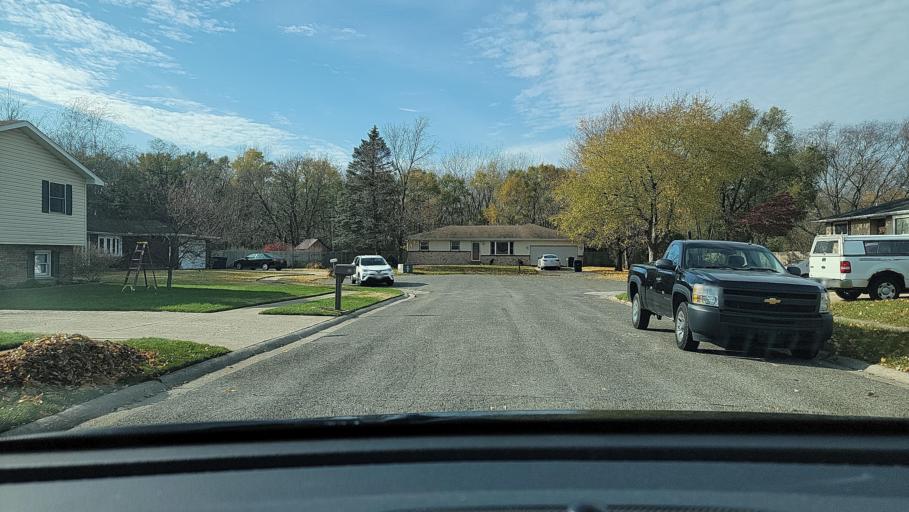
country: US
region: Indiana
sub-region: Lake County
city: Lake Station
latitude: 41.5803
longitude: -87.2111
